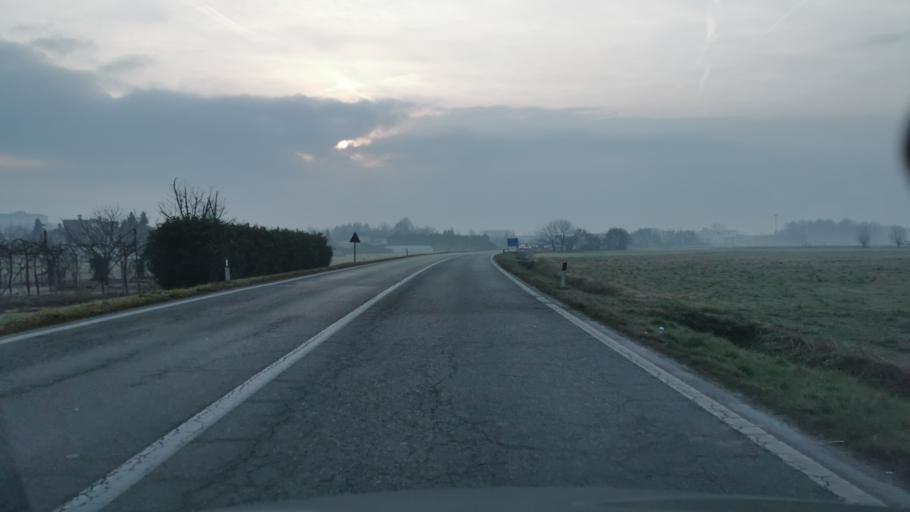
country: IT
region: Piedmont
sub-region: Provincia di Torino
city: San Giorgio Canavese
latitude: 45.3371
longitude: 7.7837
